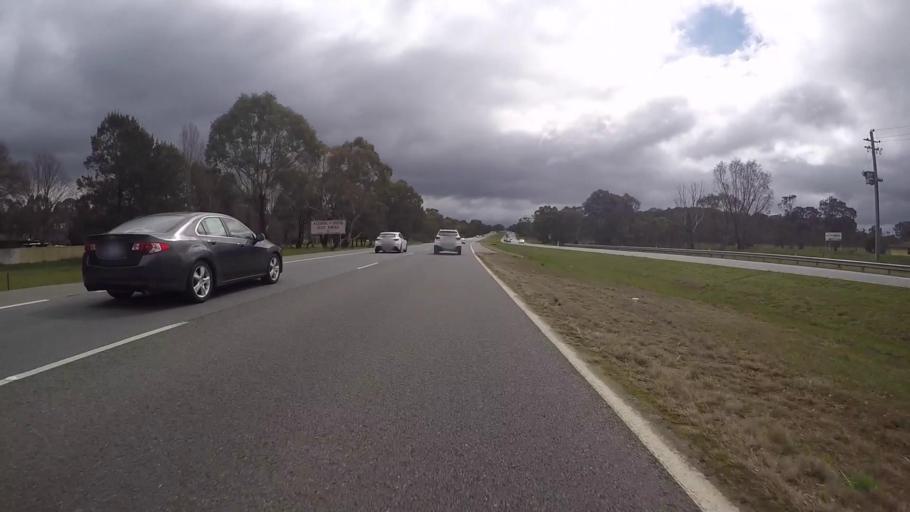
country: AU
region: Australian Capital Territory
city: Kaleen
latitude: -35.2158
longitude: 149.1150
